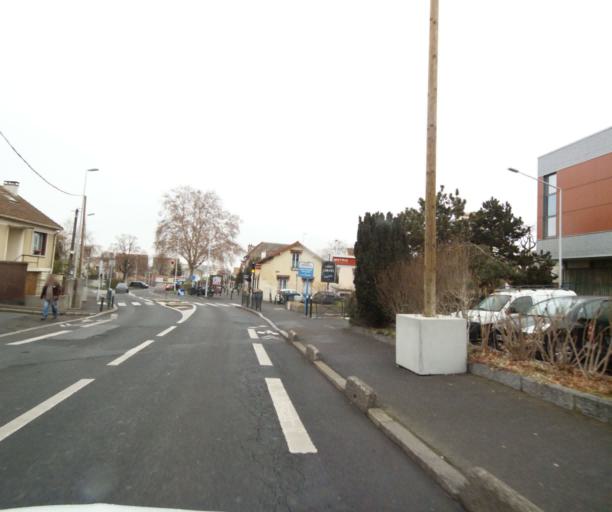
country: FR
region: Ile-de-France
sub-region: Departement des Hauts-de-Seine
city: Nanterre
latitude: 48.8886
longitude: 2.2054
